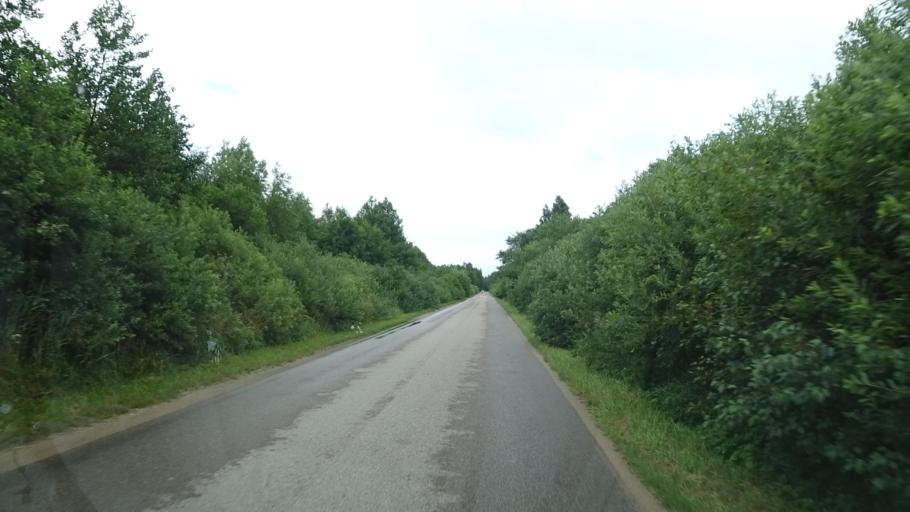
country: LV
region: Liepaja
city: Vec-Liepaja
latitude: 56.5986
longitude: 21.0300
